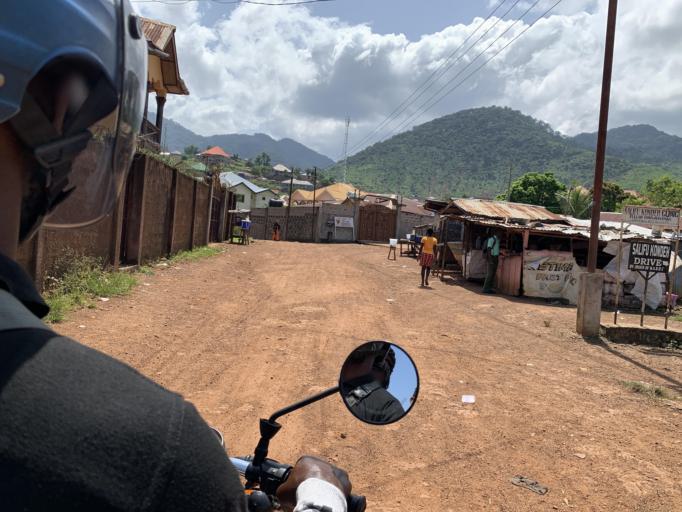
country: SL
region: Western Area
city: Hastings
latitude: 8.3741
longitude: -13.1327
